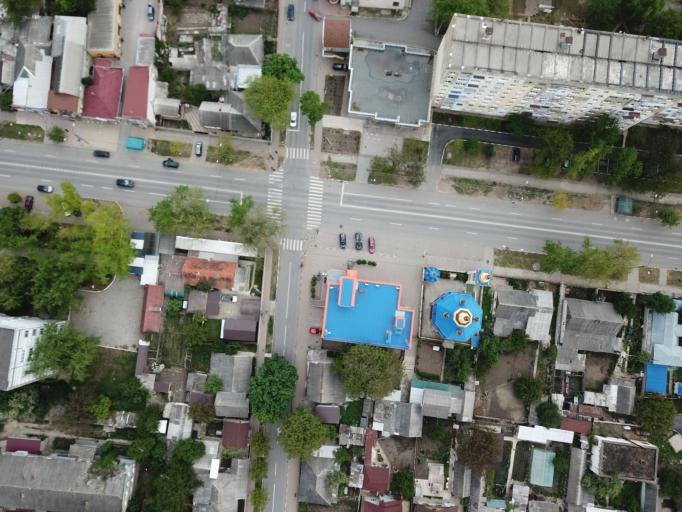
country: MD
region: Ungheni
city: Ungheni
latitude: 47.2094
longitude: 27.7964
